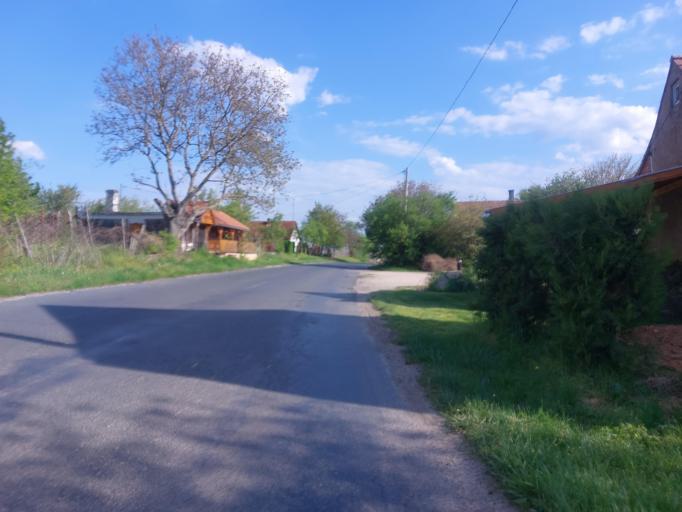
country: HU
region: Veszprem
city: Devecser
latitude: 47.1407
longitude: 17.3574
